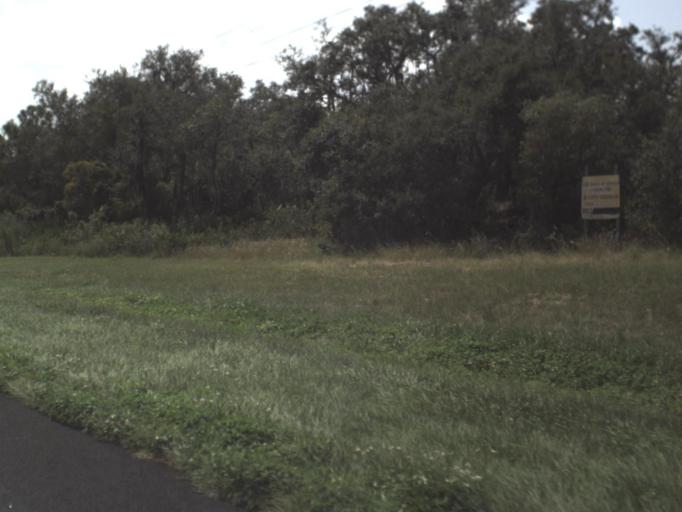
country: US
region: Florida
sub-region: Polk County
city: Frostproof
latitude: 27.6743
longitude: -81.5513
